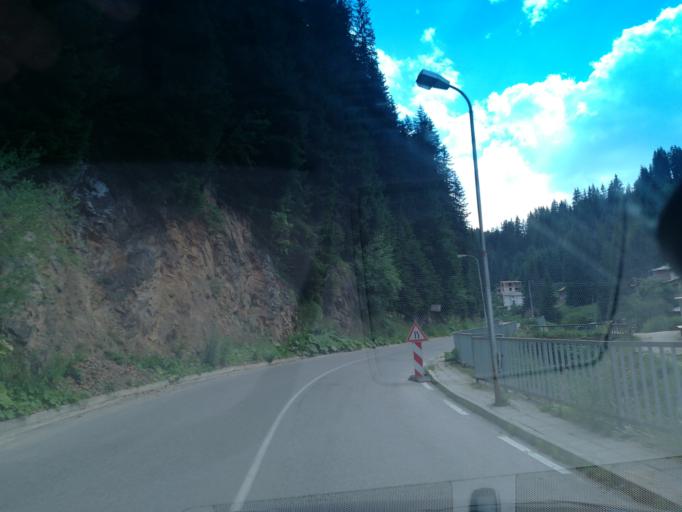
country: BG
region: Smolyan
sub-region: Obshtina Chepelare
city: Chepelare
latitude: 41.6612
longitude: 24.6341
